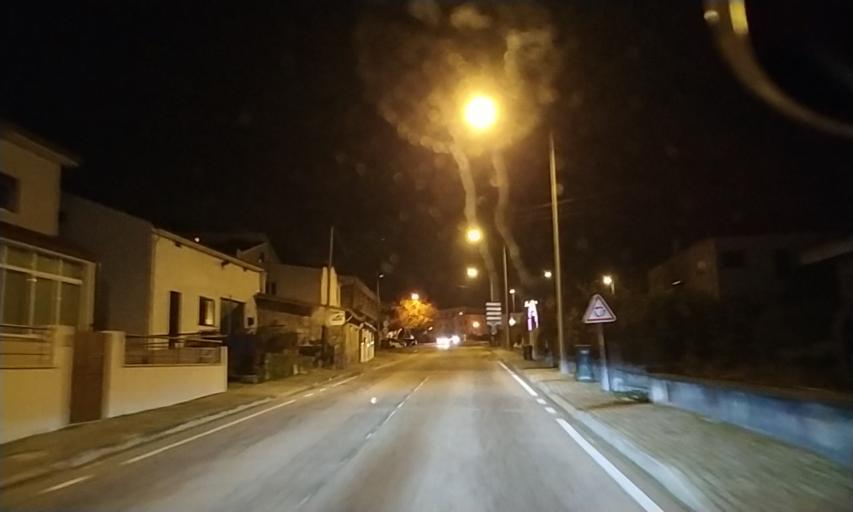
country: PT
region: Vila Real
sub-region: Sabrosa
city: Sabrosa
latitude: 41.2769
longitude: -7.4703
